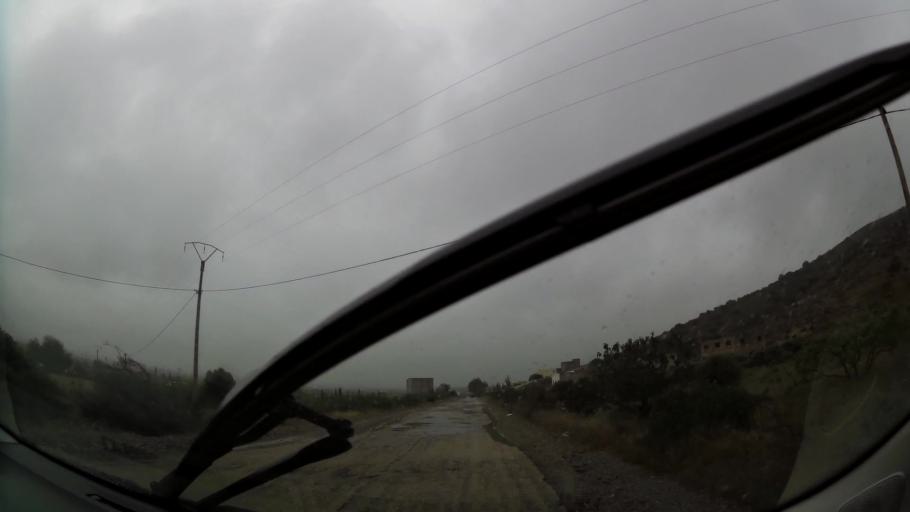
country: MA
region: Taza-Al Hoceima-Taounate
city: Imzourene
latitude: 35.1293
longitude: -3.7801
